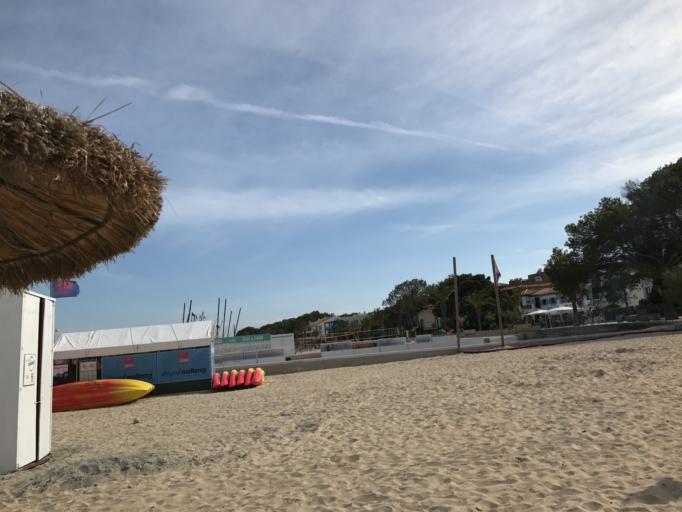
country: ES
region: Balearic Islands
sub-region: Illes Balears
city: Alcudia
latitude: 39.9027
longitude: 3.0806
